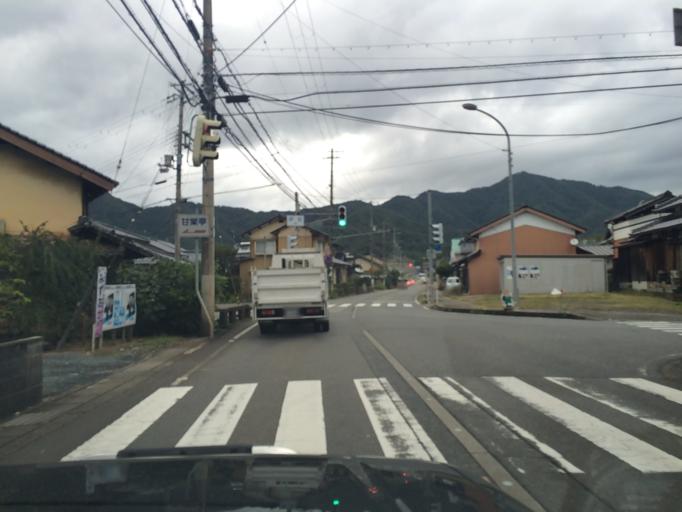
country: JP
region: Hyogo
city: Toyooka
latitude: 35.4292
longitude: 134.7950
